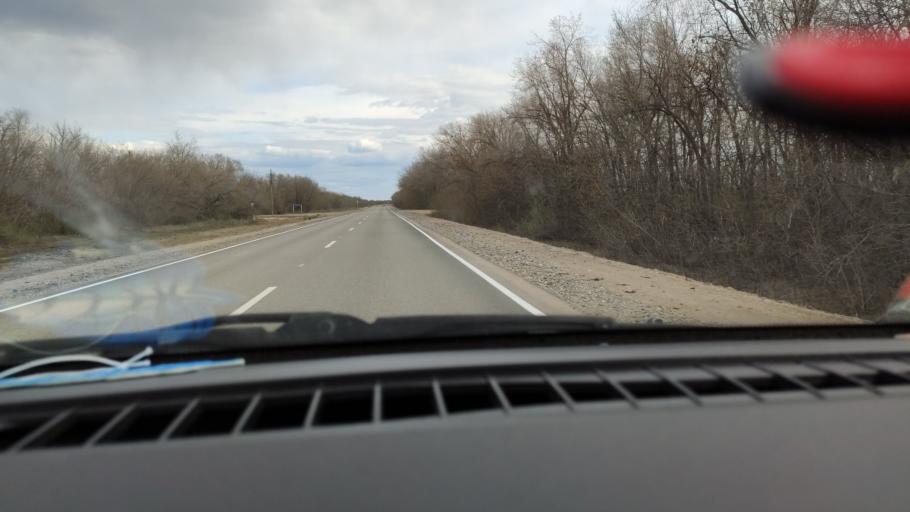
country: RU
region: Saratov
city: Privolzhskiy
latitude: 51.1636
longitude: 45.9509
